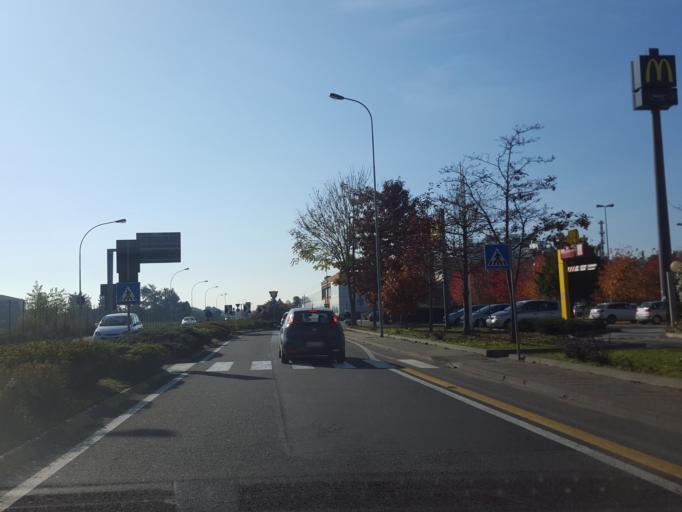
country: IT
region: Veneto
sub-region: Provincia di Vicenza
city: Brendola
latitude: 45.4936
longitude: 11.4298
